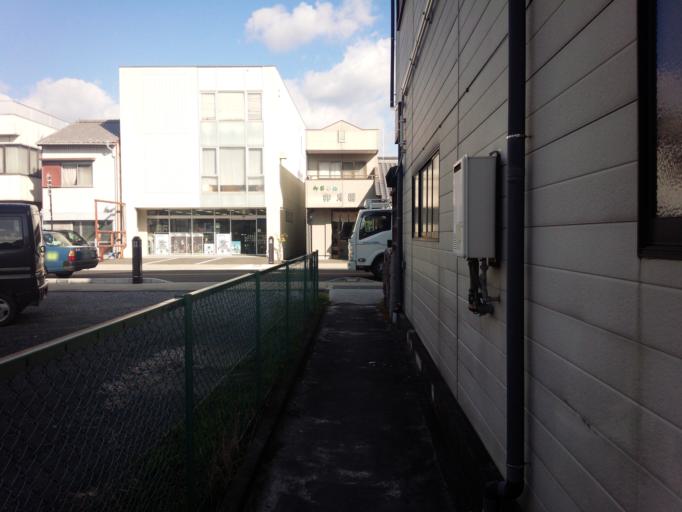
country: JP
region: Shizuoka
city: Kosai-shi
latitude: 34.6948
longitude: 137.5595
